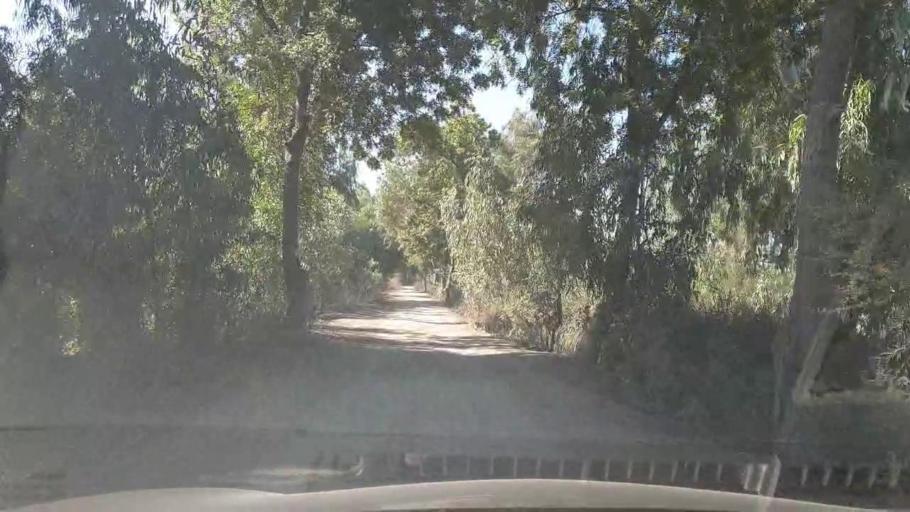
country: PK
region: Sindh
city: Mirpur Mathelo
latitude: 28.0592
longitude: 69.5048
